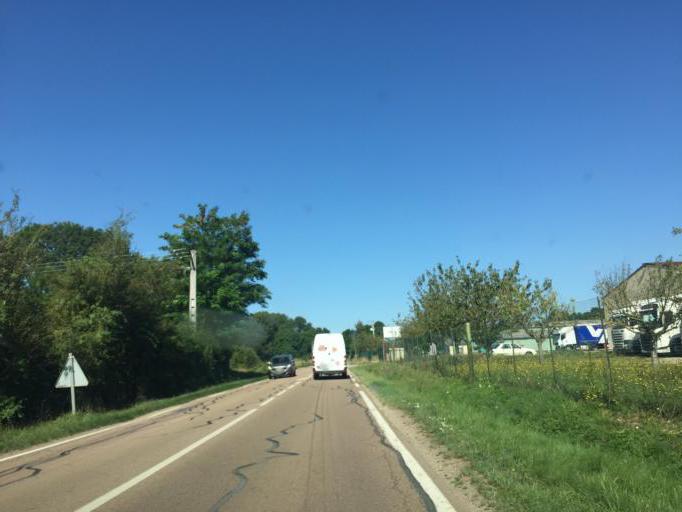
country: FR
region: Bourgogne
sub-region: Departement de la Nievre
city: Clamecy
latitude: 47.4490
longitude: 3.4859
